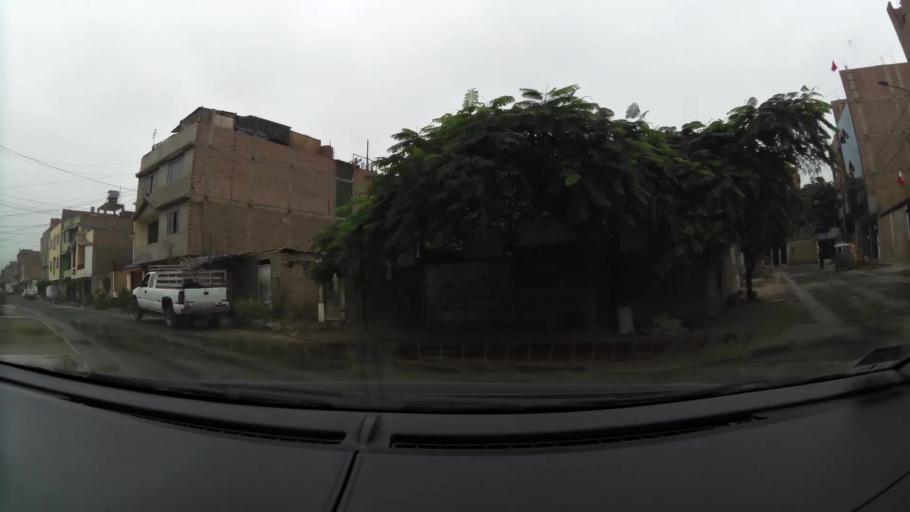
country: PE
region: Lima
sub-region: Lima
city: Independencia
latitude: -11.9758
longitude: -77.0751
